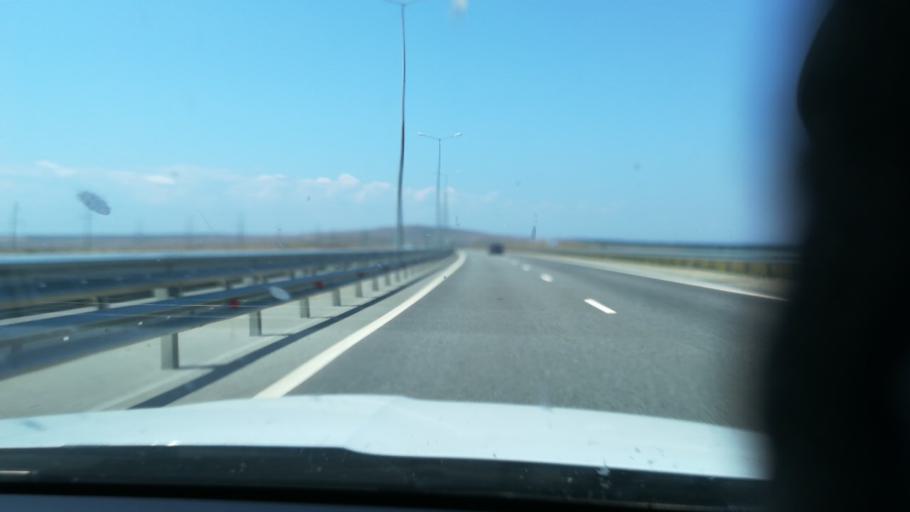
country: RU
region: Krasnodarskiy
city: Vyshestebliyevskaya
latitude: 45.2295
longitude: 36.9505
